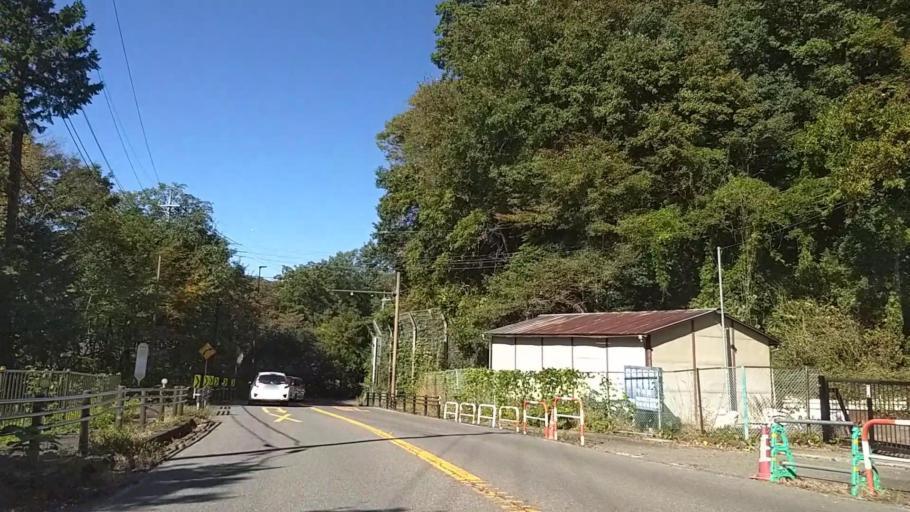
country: JP
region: Yamanashi
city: Uenohara
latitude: 35.6157
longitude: 139.2159
